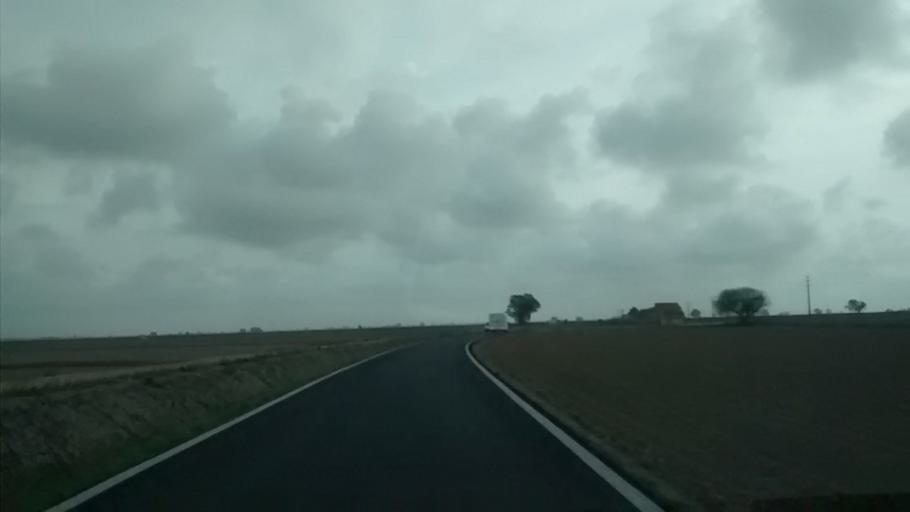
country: ES
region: Catalonia
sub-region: Provincia de Tarragona
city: Deltebre
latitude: 40.6775
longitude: 0.6631
